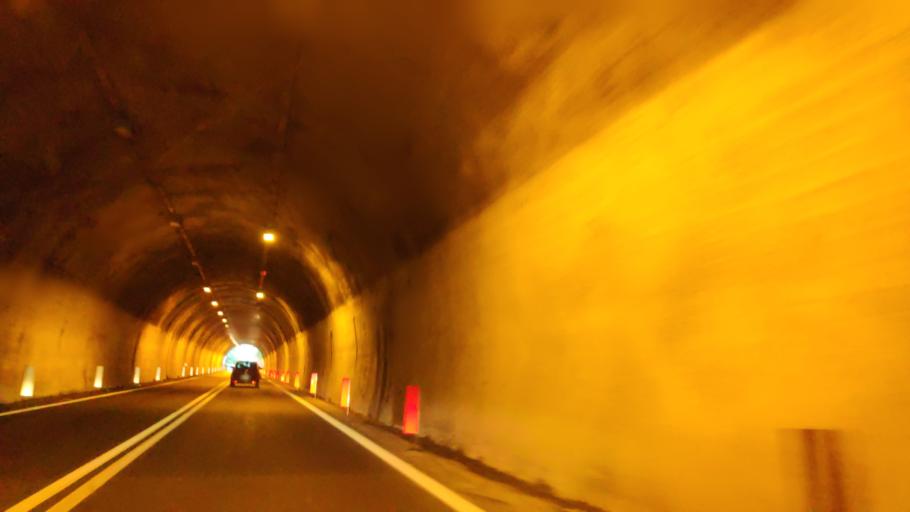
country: IT
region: Calabria
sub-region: Provincia di Reggio Calabria
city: Scilla
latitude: 38.2511
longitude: 15.7258
